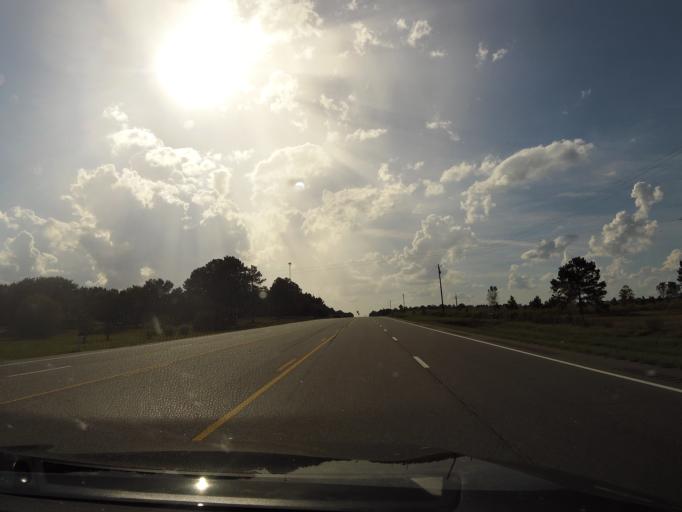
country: US
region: Georgia
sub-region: Brooks County
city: Quitman
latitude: 30.7857
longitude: -83.6009
